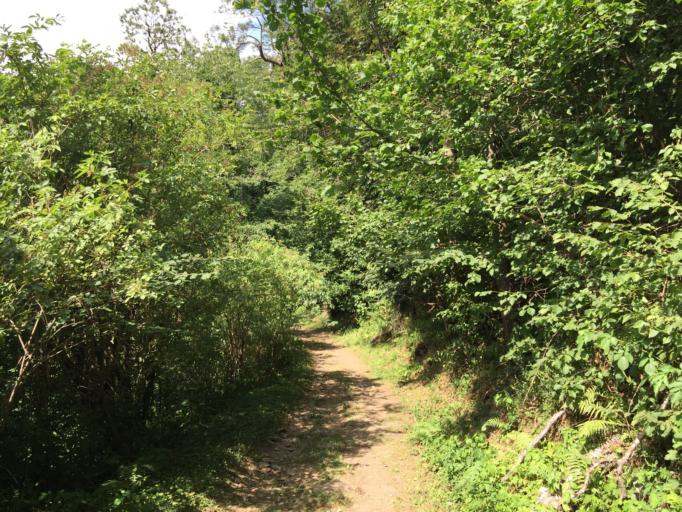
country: FR
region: Rhone-Alpes
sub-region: Departement de la Loire
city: Saint-Chamond
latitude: 45.4237
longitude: 4.5150
